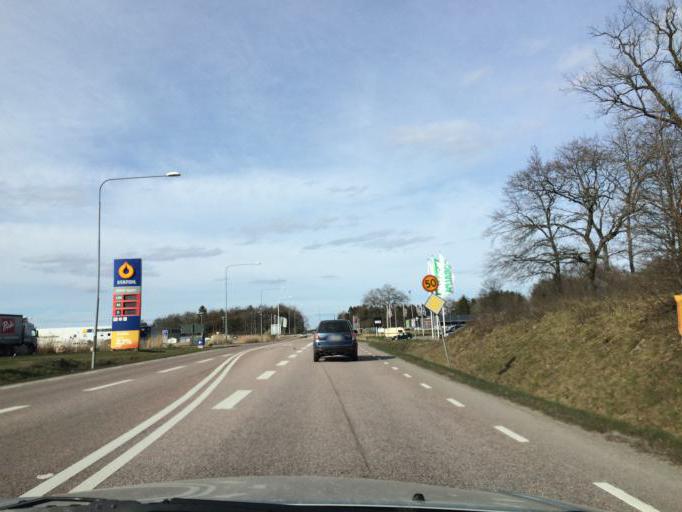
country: SE
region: Soedermanland
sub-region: Eskilstuna Kommun
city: Torshalla
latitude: 59.3944
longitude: 16.4683
